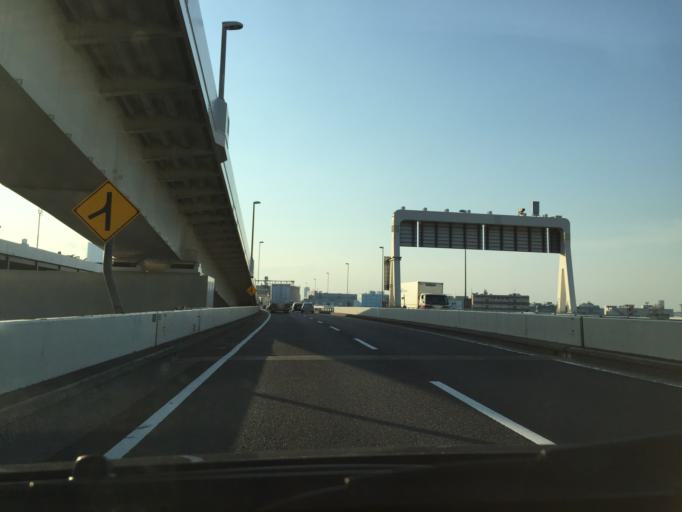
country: JP
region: Kanagawa
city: Yokohama
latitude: 35.4398
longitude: 139.6611
